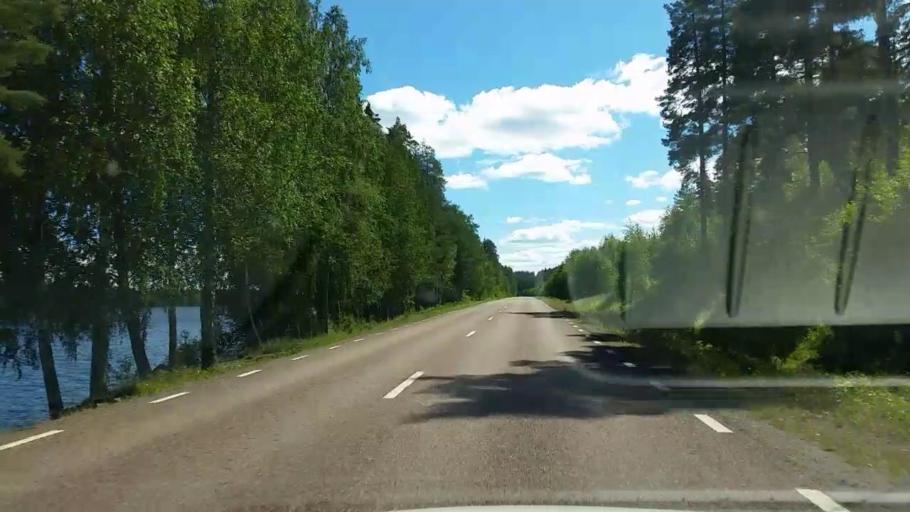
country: SE
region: Dalarna
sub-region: Faluns Kommun
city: Svardsjo
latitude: 60.9659
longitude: 15.6920
